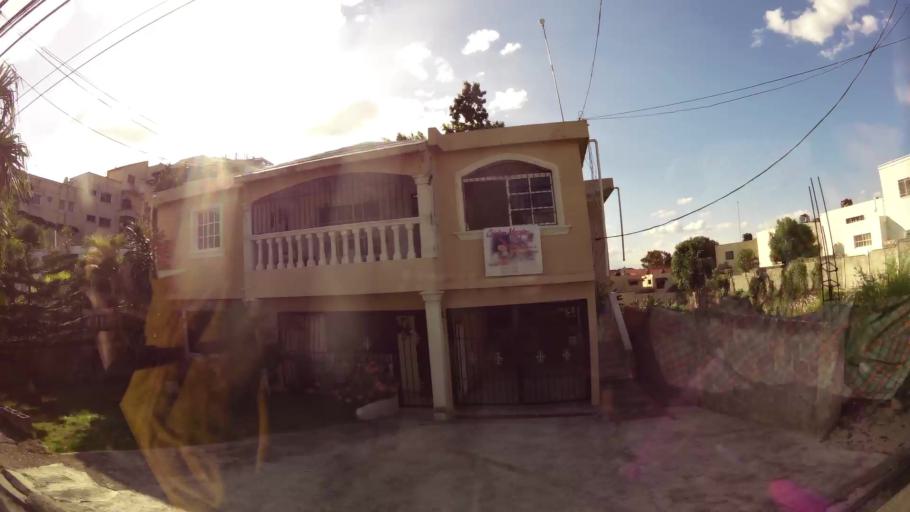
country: DO
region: Nacional
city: Santo Domingo
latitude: 18.5079
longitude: -69.9765
